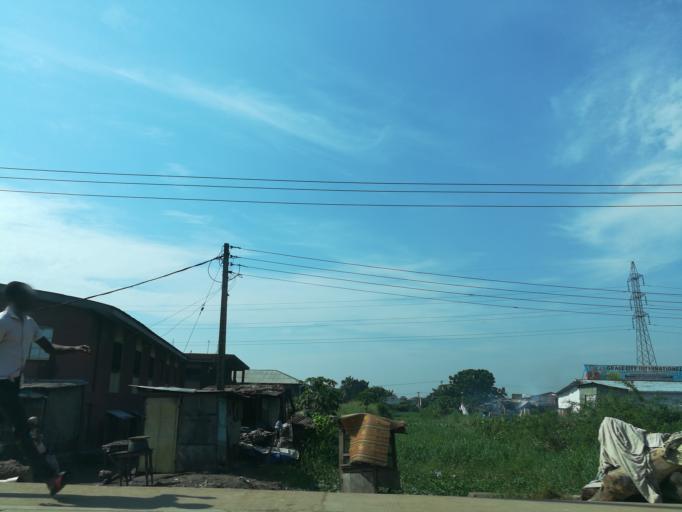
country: NG
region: Lagos
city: Ojota
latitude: 6.6093
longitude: 3.4292
